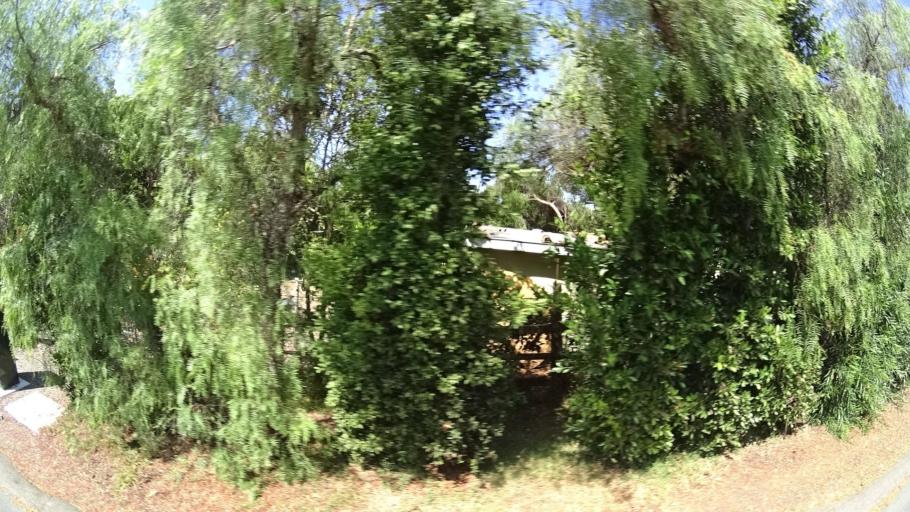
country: US
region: California
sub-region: San Diego County
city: Rancho Santa Fe
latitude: 33.0281
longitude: -117.2295
